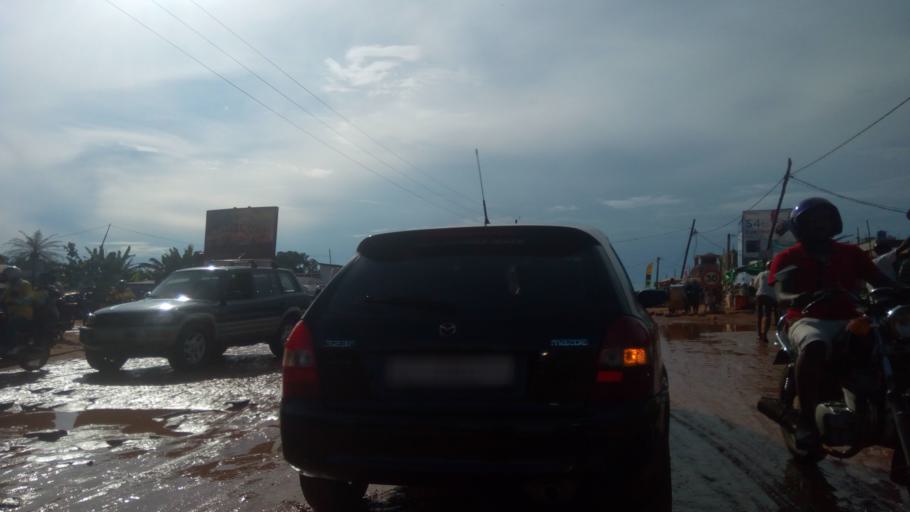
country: BJ
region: Atlantique
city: Abomey-Calavi
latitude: 6.4530
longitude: 2.3379
